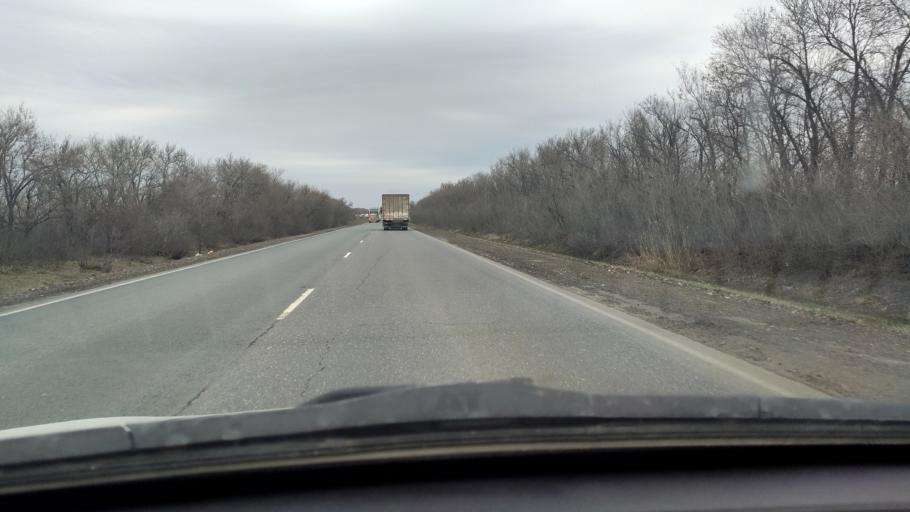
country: RU
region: Samara
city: Zhigulevsk
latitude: 53.2987
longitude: 49.3409
